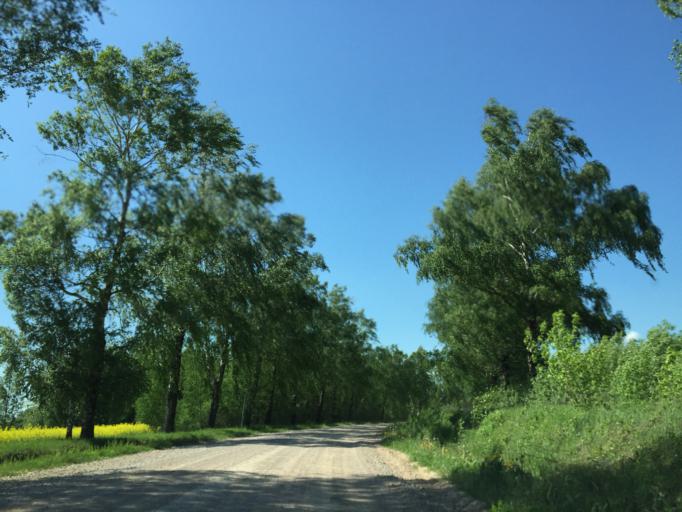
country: LV
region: Rundales
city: Pilsrundale
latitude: 56.5347
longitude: 24.0008
